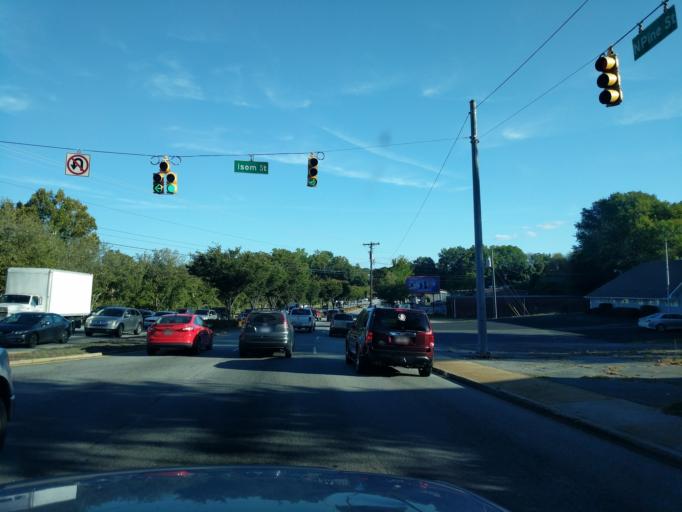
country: US
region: South Carolina
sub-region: Spartanburg County
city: Spartanburg
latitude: 34.9634
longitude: -81.9272
